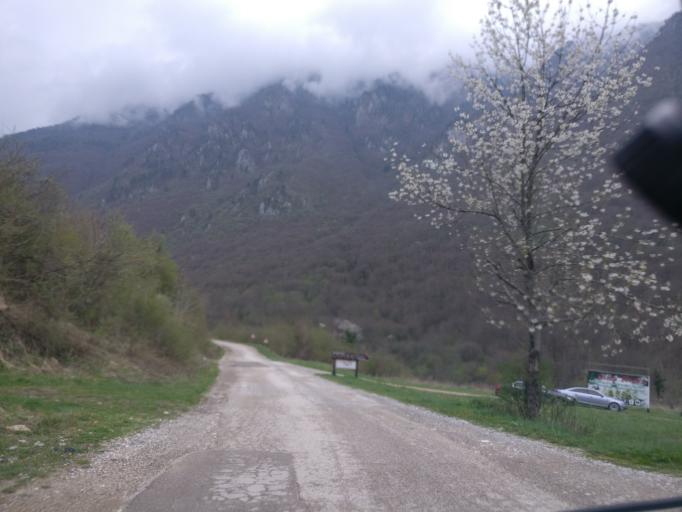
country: BA
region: Republika Srpska
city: Foca
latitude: 43.3607
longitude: 18.8122
